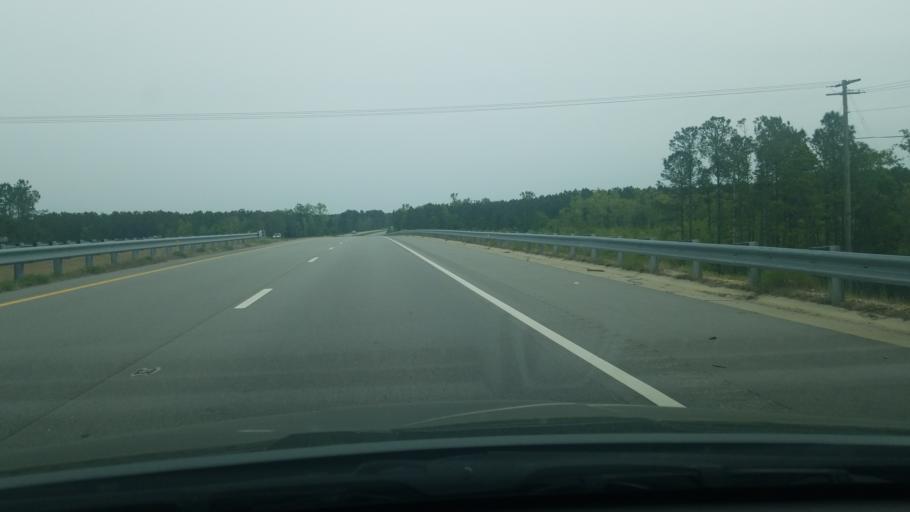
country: US
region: North Carolina
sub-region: Craven County
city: River Bend
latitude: 35.0286
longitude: -77.2256
